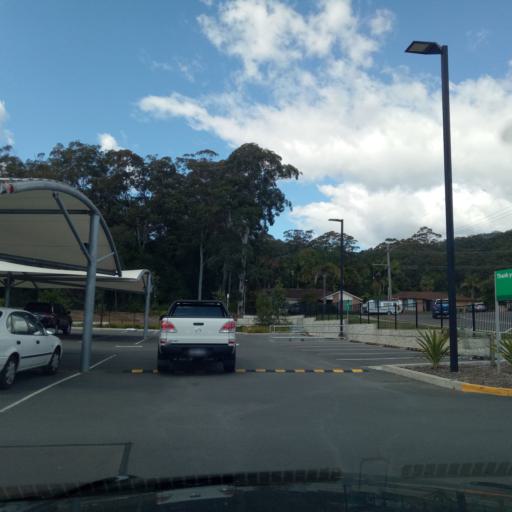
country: AU
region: New South Wales
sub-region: Gosford Shire
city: Lisarow
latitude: -33.3863
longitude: 151.3664
